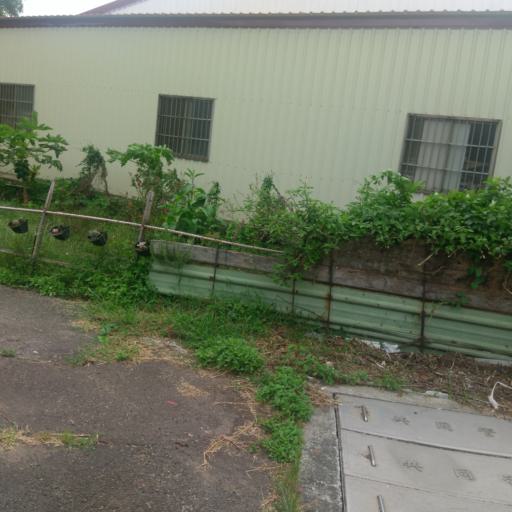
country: TW
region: Taiwan
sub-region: Hsinchu
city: Hsinchu
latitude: 24.7508
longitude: 120.9055
